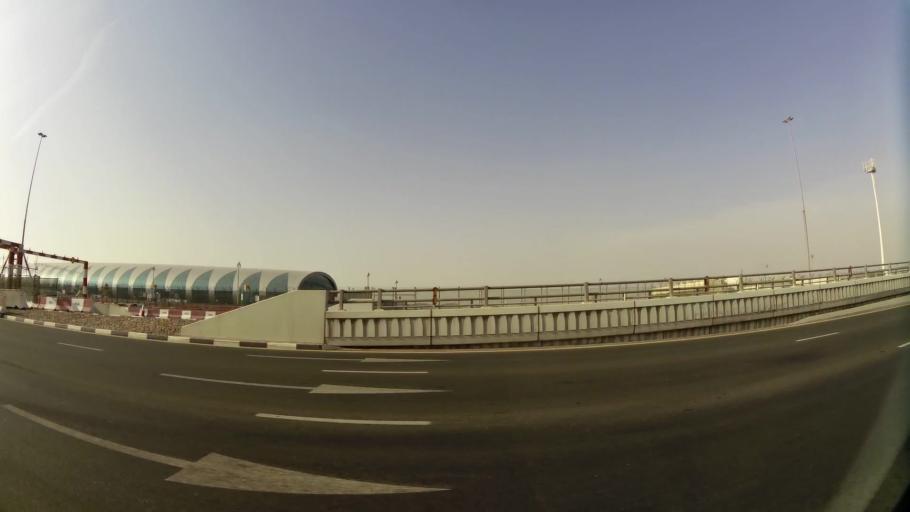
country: AE
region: Ash Shariqah
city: Sharjah
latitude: 25.2385
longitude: 55.3745
